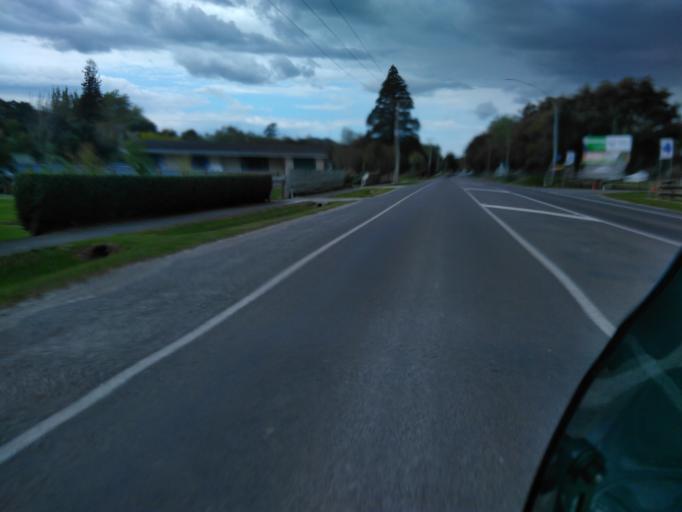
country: NZ
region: Gisborne
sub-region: Gisborne District
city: Gisborne
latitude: -38.6487
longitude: 177.9785
